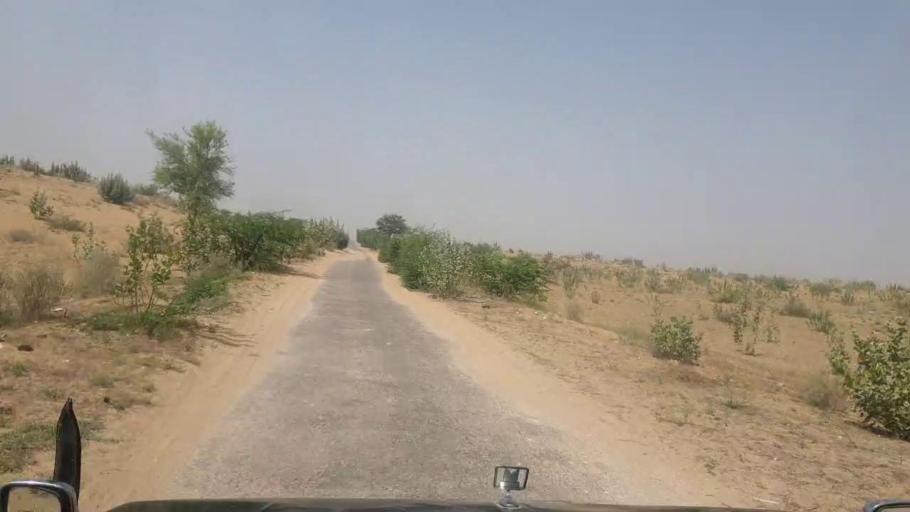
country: PK
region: Sindh
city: Islamkot
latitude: 25.1183
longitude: 70.2360
